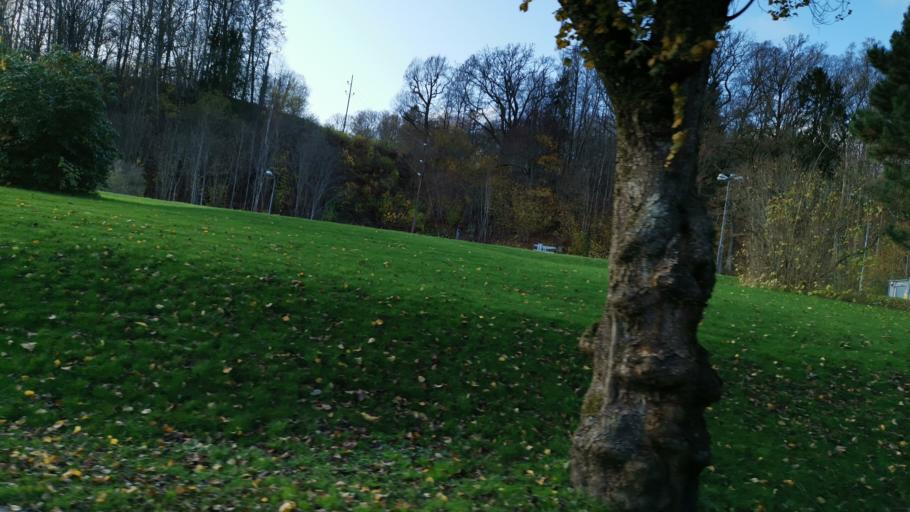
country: SE
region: Vaestra Goetaland
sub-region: Munkedals Kommun
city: Munkedal
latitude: 58.4810
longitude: 11.6921
